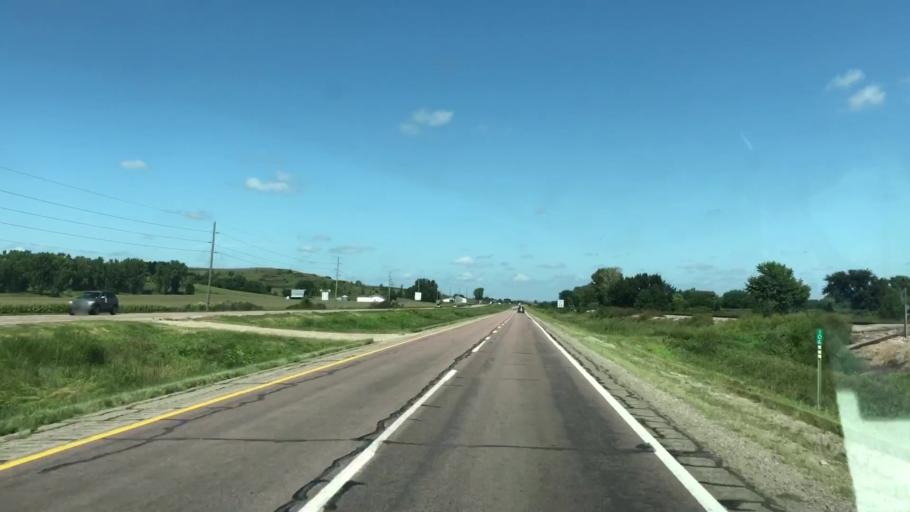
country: US
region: Iowa
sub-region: Woodbury County
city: Sioux City
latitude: 42.6349
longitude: -96.2897
